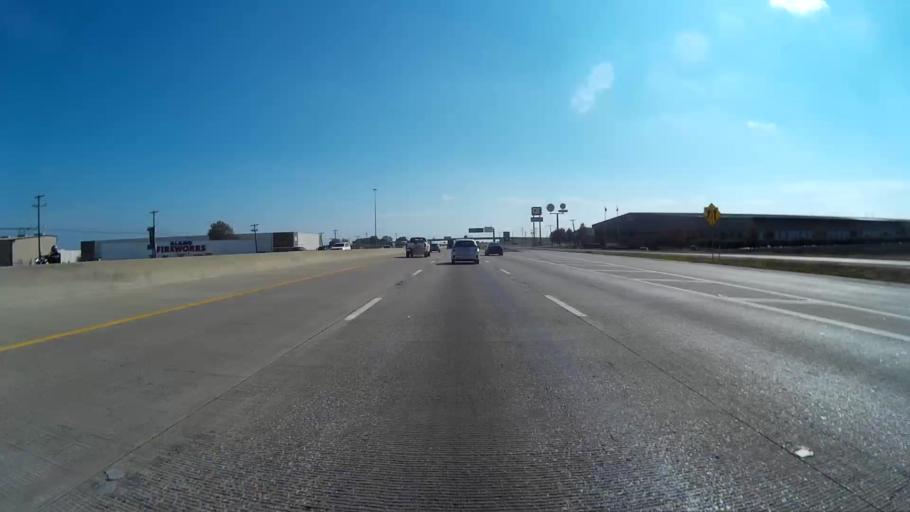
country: US
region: Texas
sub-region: Dallas County
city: Hutchins
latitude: 32.6364
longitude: -96.7014
